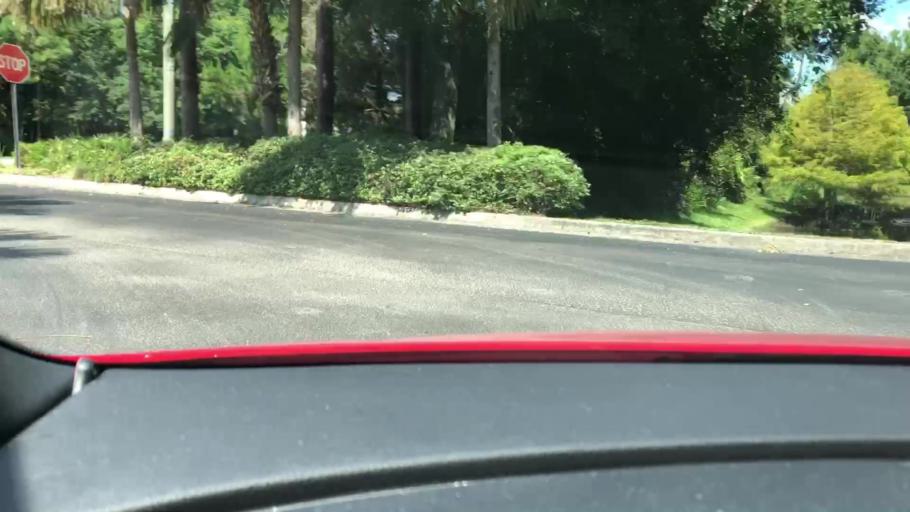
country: US
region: Florida
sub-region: Volusia County
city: Port Orange
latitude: 29.1134
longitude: -81.0269
